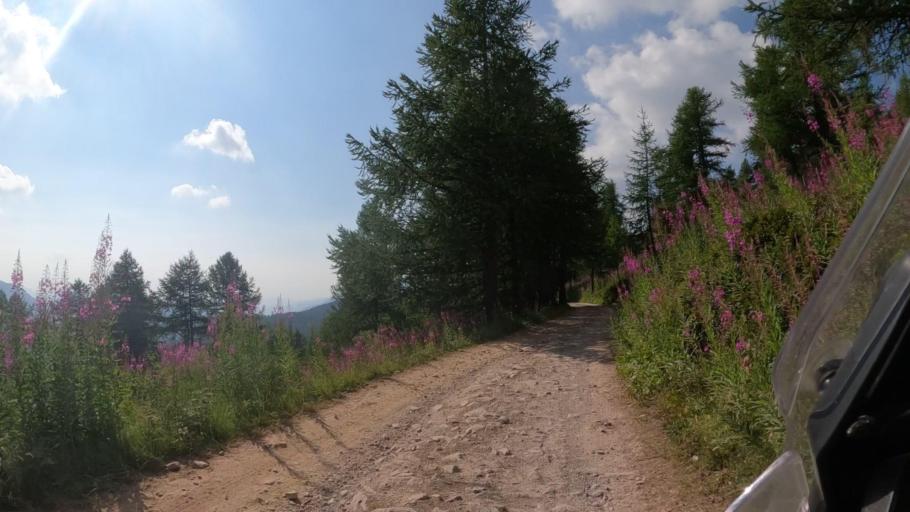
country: IT
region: Piedmont
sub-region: Provincia di Cuneo
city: Briga Alta
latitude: 44.1277
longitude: 7.6909
